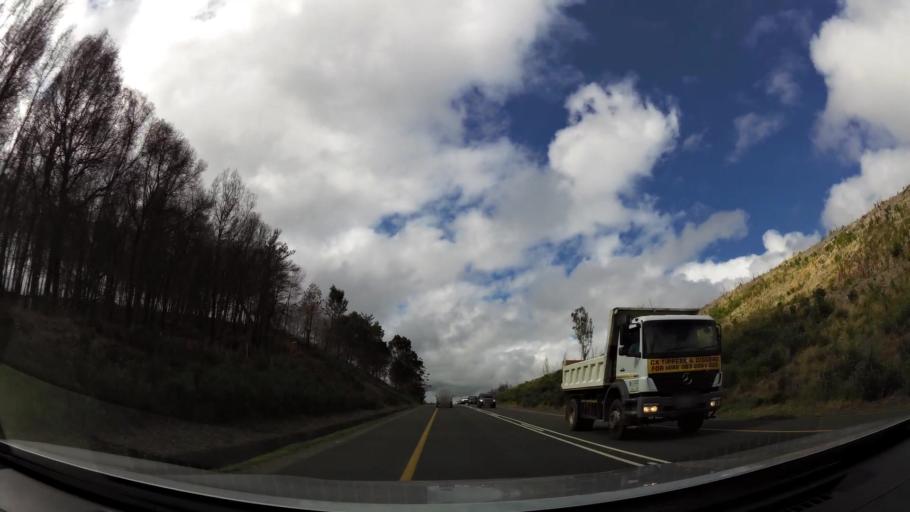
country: ZA
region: Western Cape
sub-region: Eden District Municipality
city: Knysna
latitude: -34.0371
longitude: 23.1461
